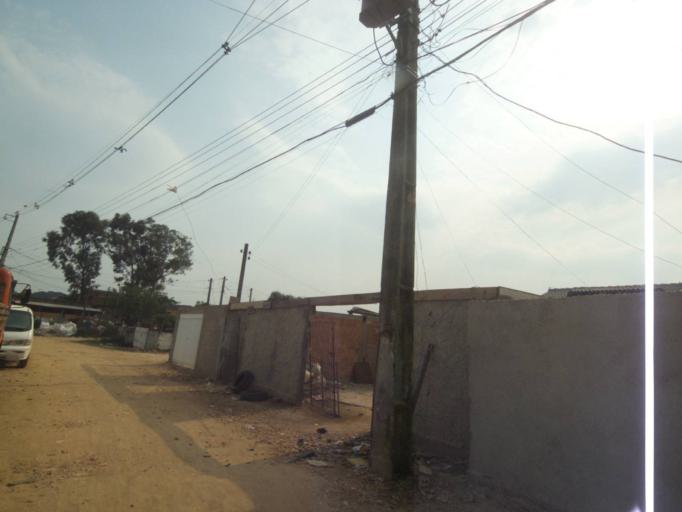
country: BR
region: Parana
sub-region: Sao Jose Dos Pinhais
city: Sao Jose dos Pinhais
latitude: -25.5384
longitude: -49.2315
